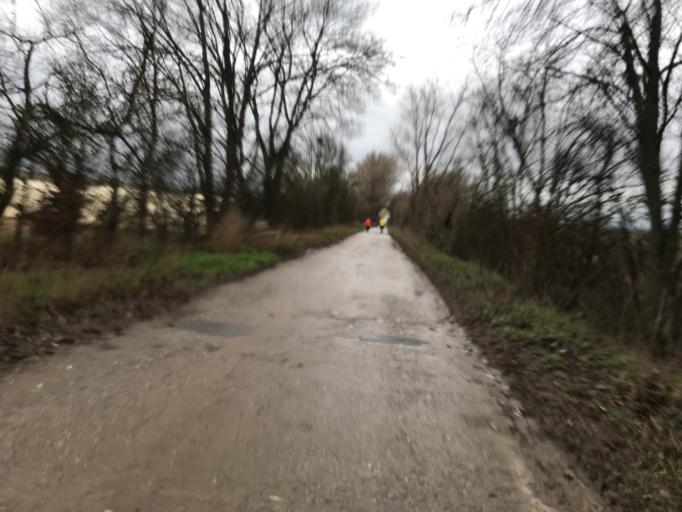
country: DE
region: Rheinland-Pfalz
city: Harxheim
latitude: 49.9197
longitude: 8.2485
